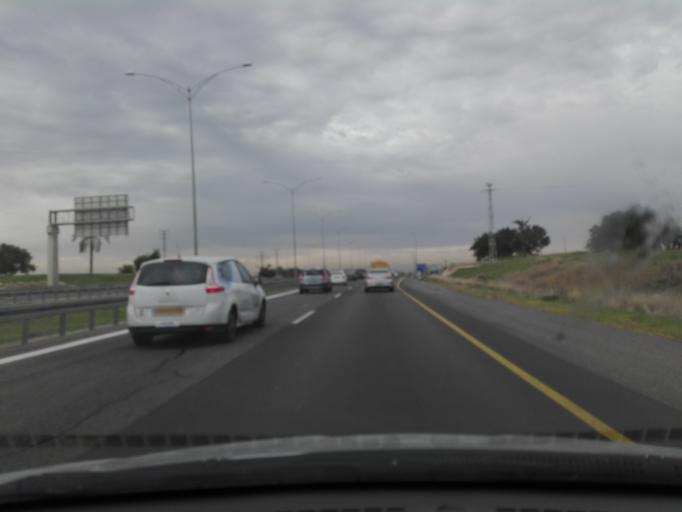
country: IL
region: Central District
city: Ramla
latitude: 31.8873
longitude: 34.8807
